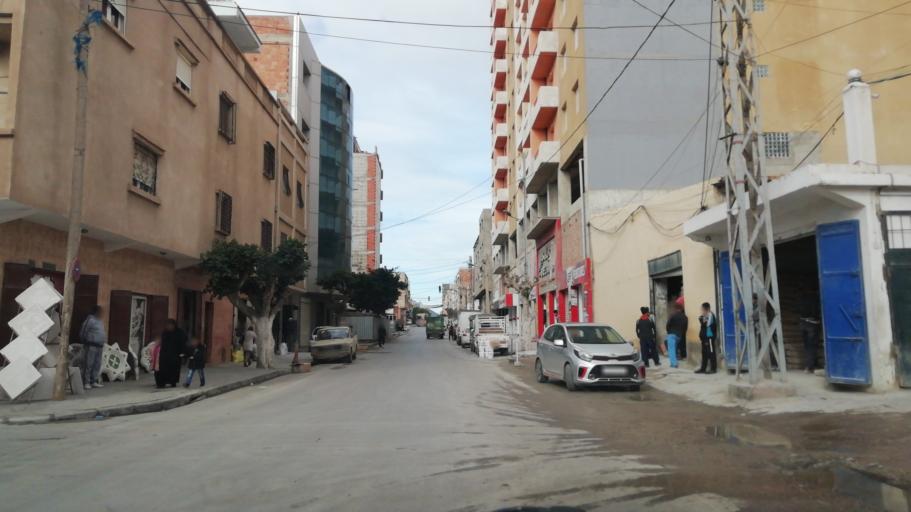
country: DZ
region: Oran
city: Oran
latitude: 35.6880
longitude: -0.6215
